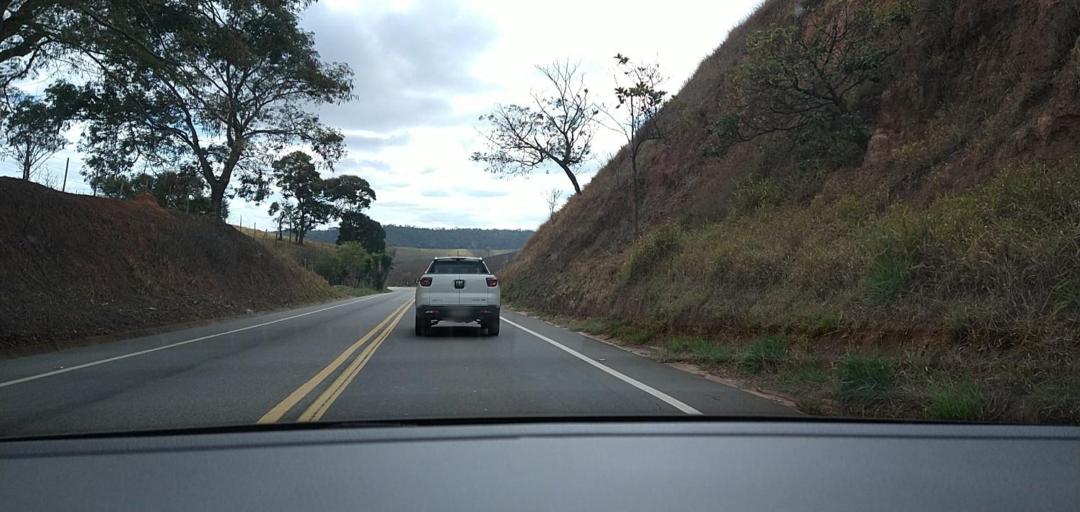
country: BR
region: Minas Gerais
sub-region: Ponte Nova
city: Ponte Nova
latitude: -20.5272
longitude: -42.8944
